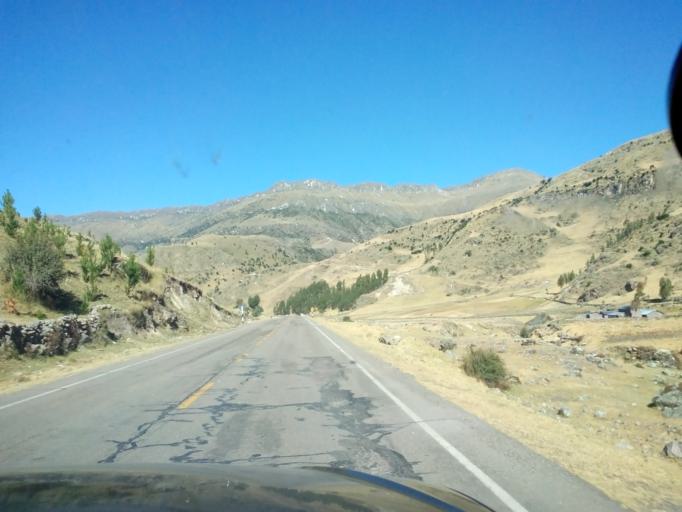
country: PE
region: Ayacucho
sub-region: Provincia de Huamanga
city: Vinchos
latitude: -13.3473
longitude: -74.4811
